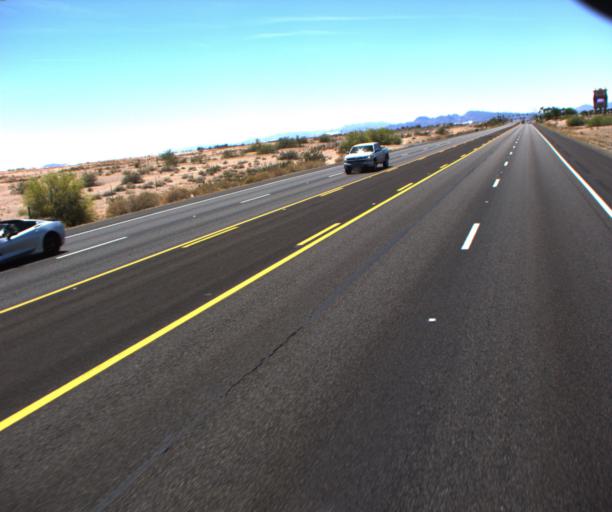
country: US
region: Arizona
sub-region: La Paz County
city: Parker
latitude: 34.1622
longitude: -114.2610
